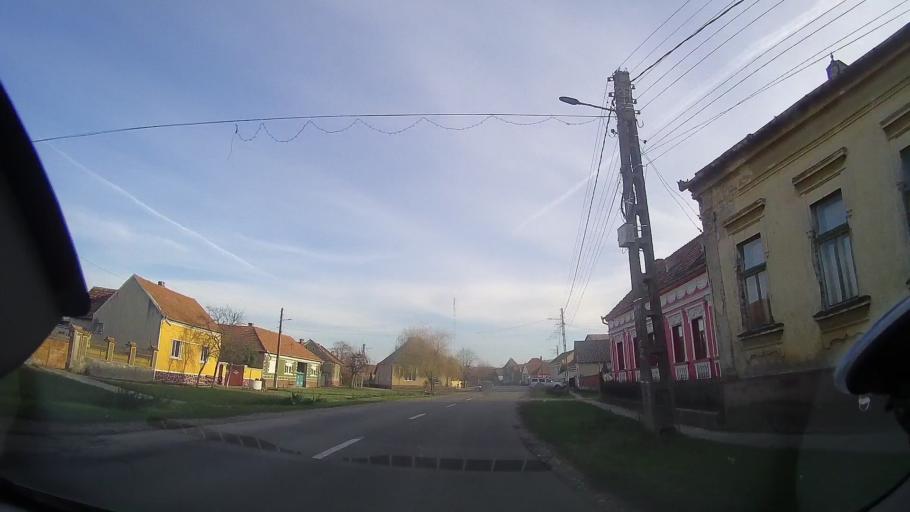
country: RO
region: Bihor
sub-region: Comuna Tetchea
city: Hotar
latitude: 47.0550
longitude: 22.2754
